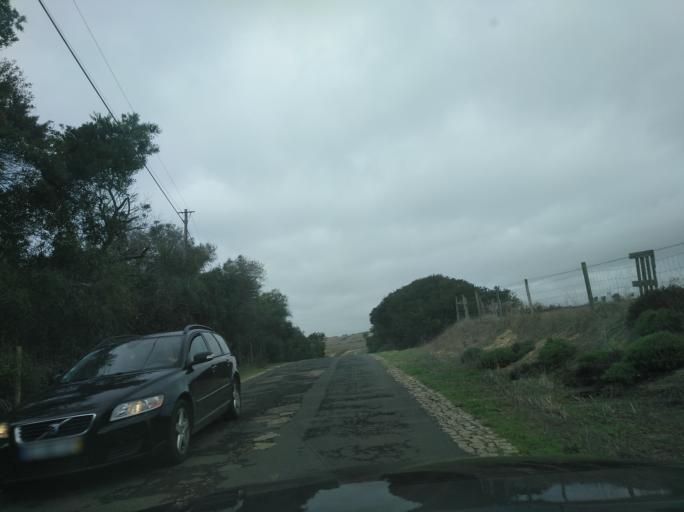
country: PT
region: Setubal
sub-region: Sines
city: Porto Covo
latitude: 37.8358
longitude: -8.7872
